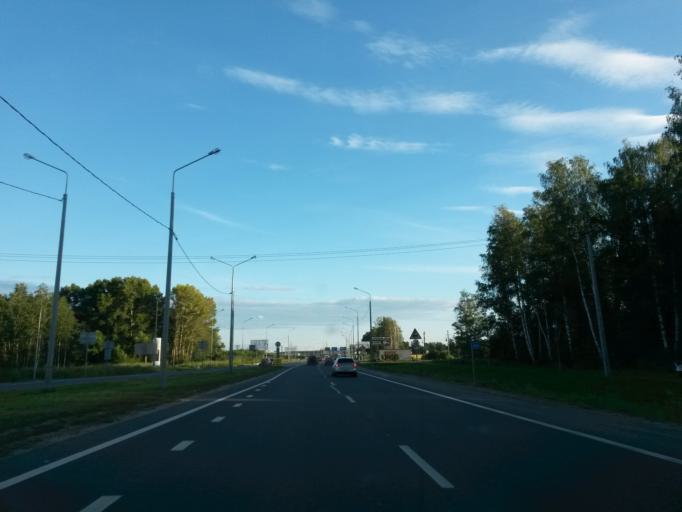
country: RU
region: Jaroslavl
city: Yaroslavl
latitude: 57.6964
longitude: 39.8988
